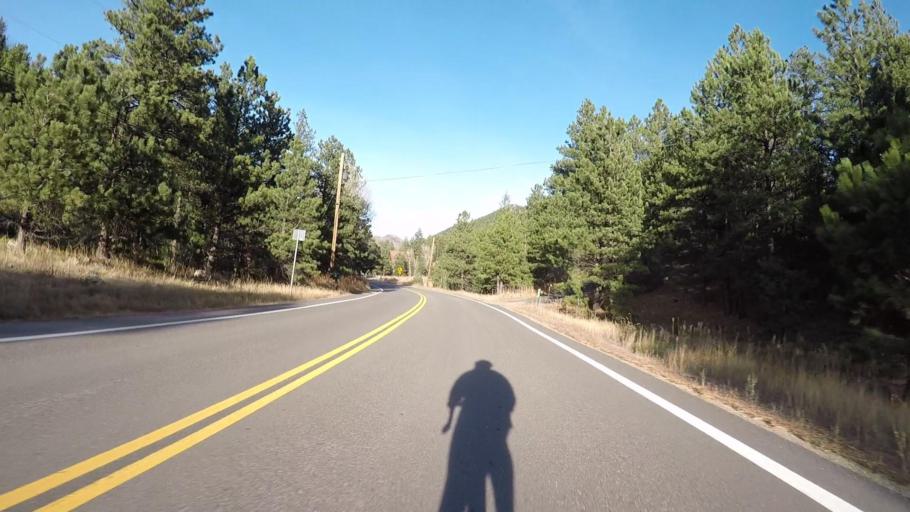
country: US
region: Colorado
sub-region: Boulder County
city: Boulder
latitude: 40.0912
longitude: -105.3537
